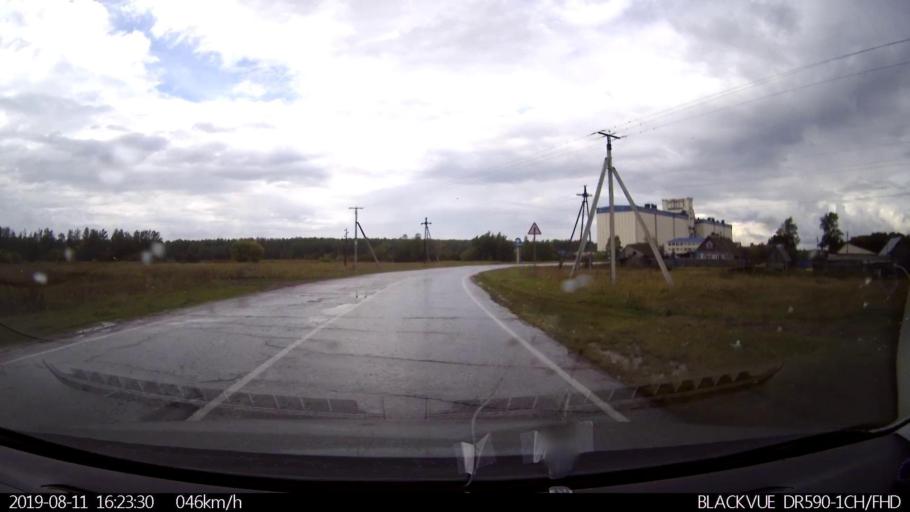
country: RU
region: Ulyanovsk
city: Mayna
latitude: 54.0955
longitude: 47.5884
